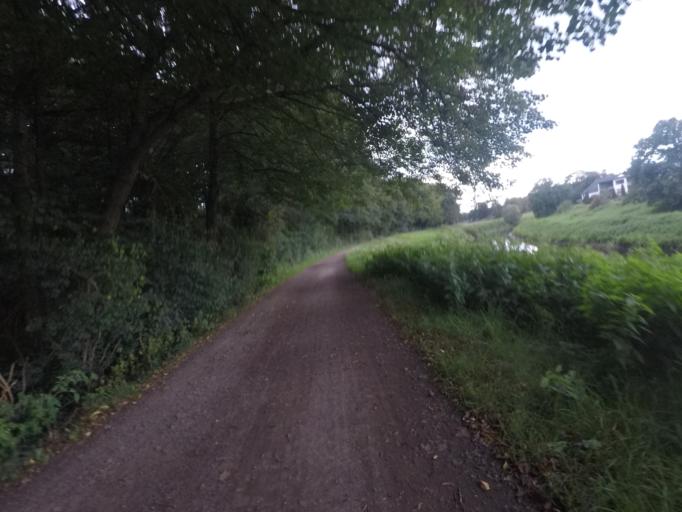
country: DE
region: North Rhine-Westphalia
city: Bad Oeynhausen
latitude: 52.2084
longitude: 8.7962
